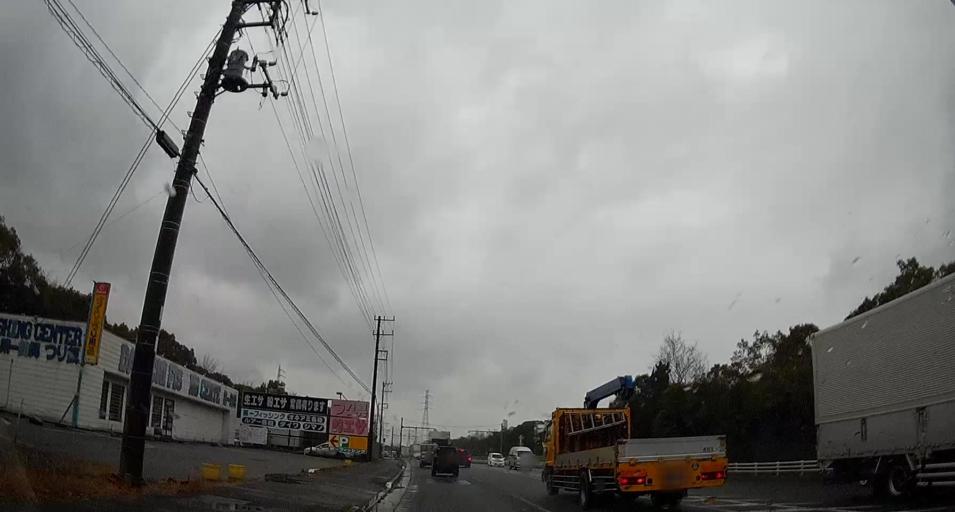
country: JP
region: Chiba
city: Ichihara
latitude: 35.5301
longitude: 140.0937
